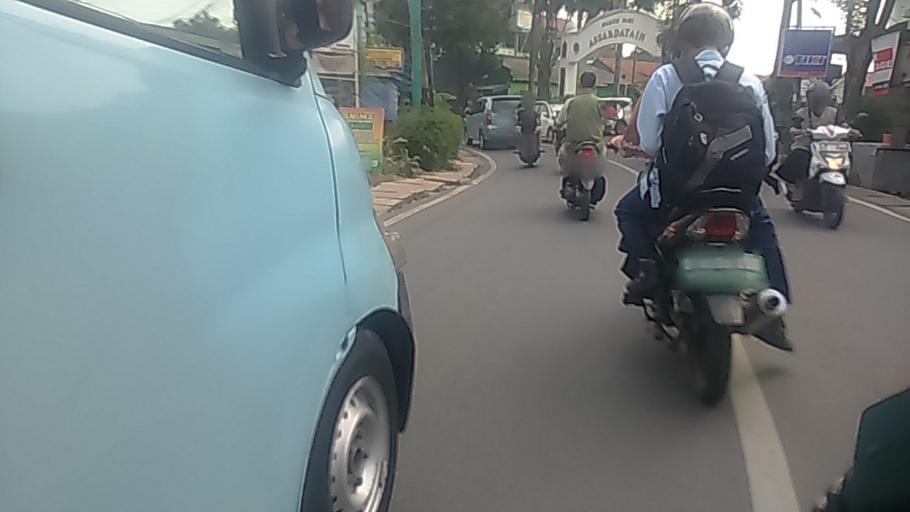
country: ID
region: West Java
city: Depok
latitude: -6.3376
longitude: 106.8056
